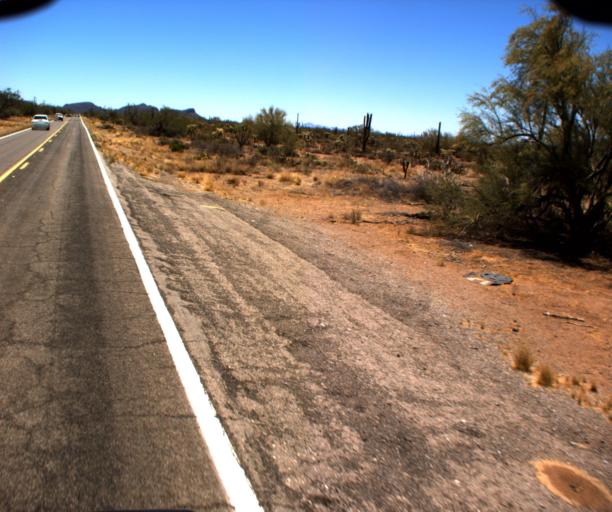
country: US
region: Arizona
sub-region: Pima County
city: Sells
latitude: 32.0132
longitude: -111.9959
